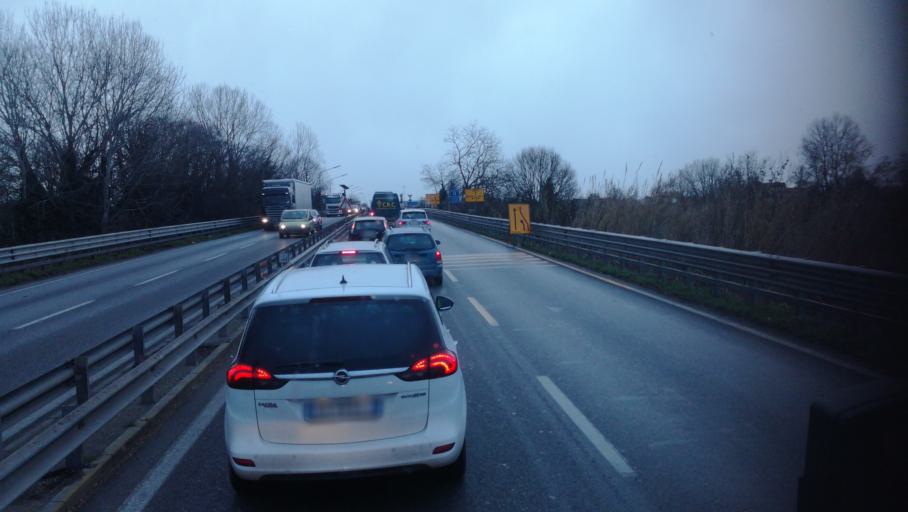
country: IT
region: Emilia-Romagna
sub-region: Provincia di Ravenna
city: Madonna Dell'Albero
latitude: 44.3851
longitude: 12.1924
